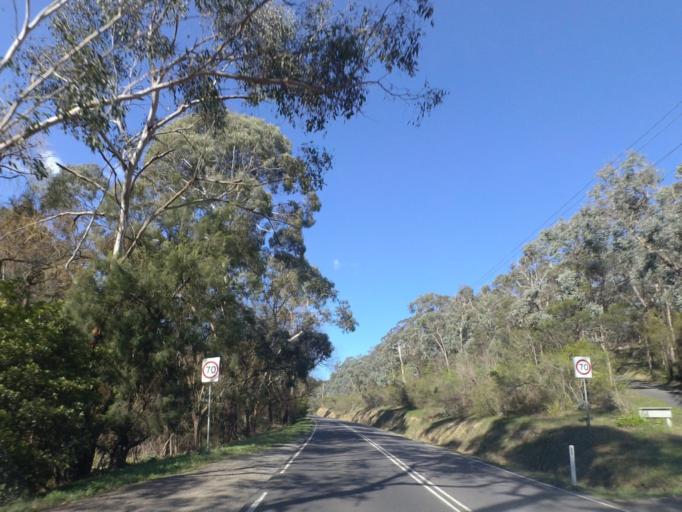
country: AU
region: Victoria
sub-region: Manningham
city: Park Orchards
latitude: -37.7714
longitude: 145.2070
